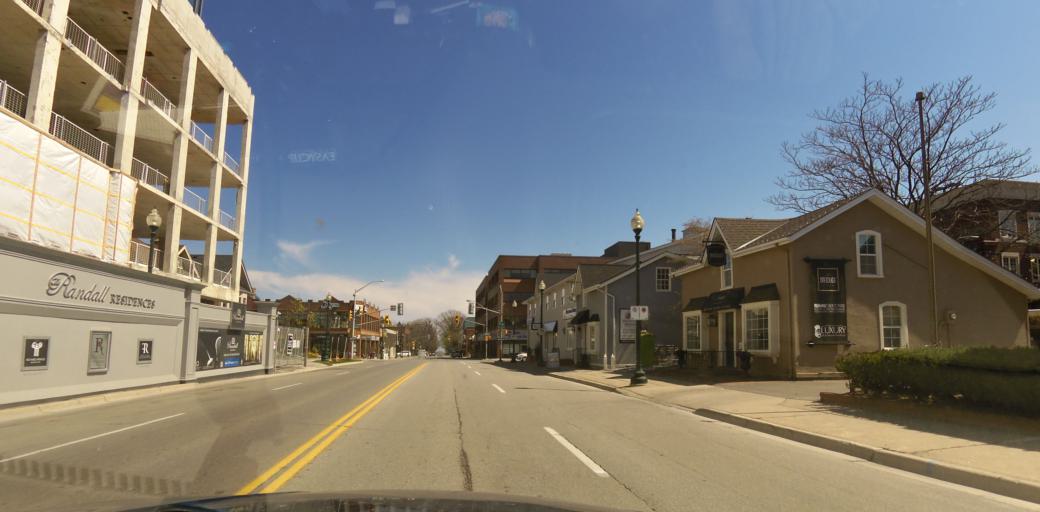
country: CA
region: Ontario
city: Oakville
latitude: 43.4484
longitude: -79.6681
